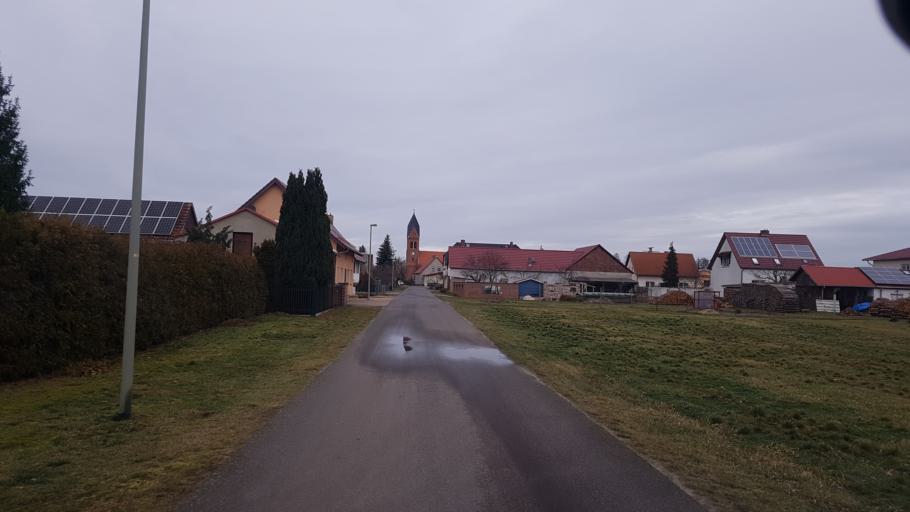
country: DE
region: Brandenburg
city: Sonnewalde
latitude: 51.6641
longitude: 13.6446
